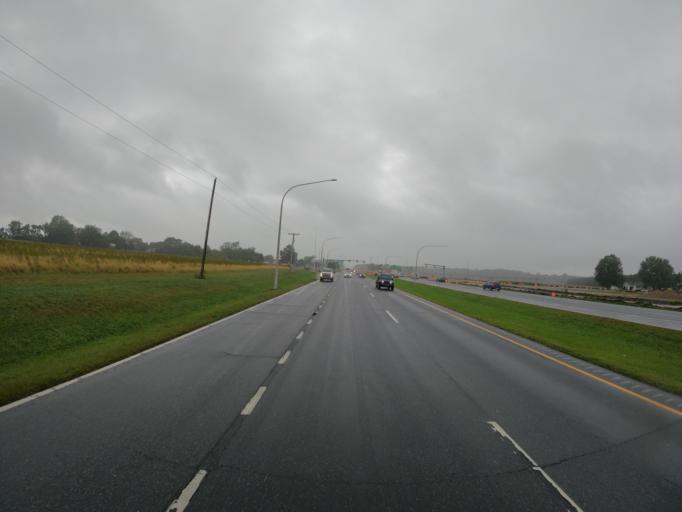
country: US
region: Delaware
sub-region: Sussex County
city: Milton
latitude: 38.8046
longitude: -75.2702
